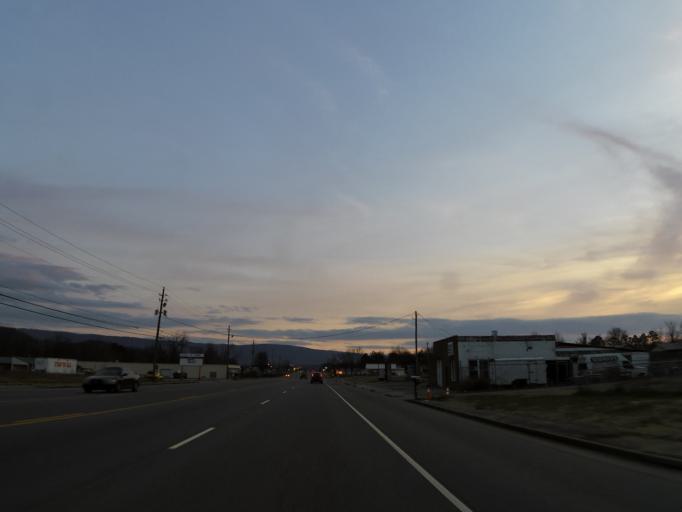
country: US
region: Tennessee
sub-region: McMinn County
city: Etowah
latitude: 35.3488
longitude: -84.5208
